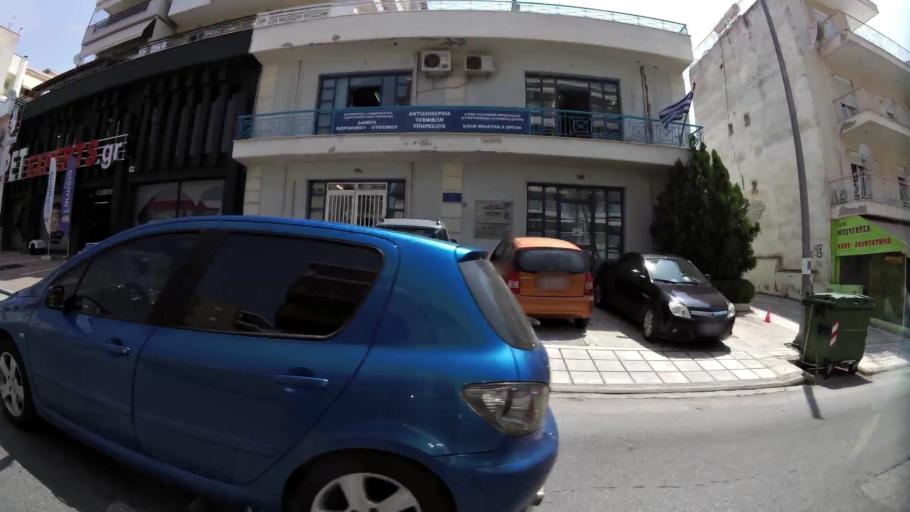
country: GR
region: Central Macedonia
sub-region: Nomos Thessalonikis
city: Evosmos
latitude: 40.6764
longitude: 22.9061
